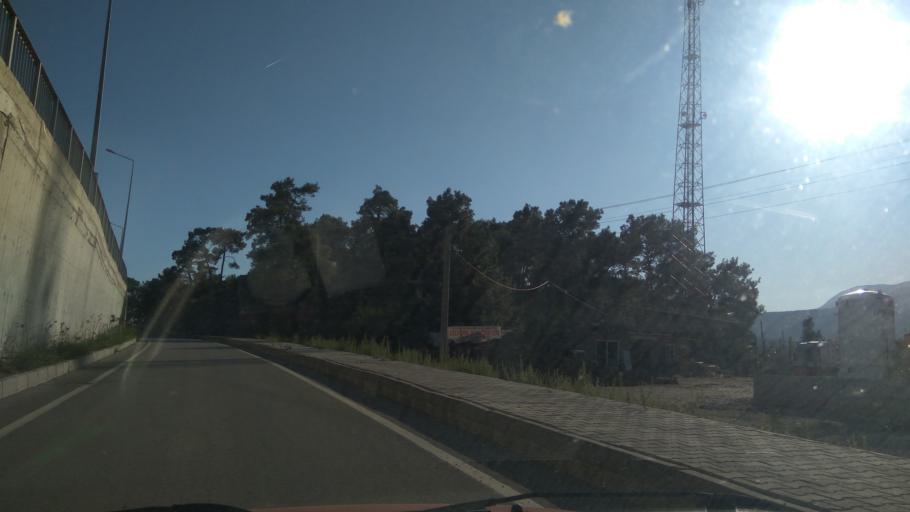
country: TR
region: Antalya
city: Kemer
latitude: 36.5906
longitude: 30.5406
